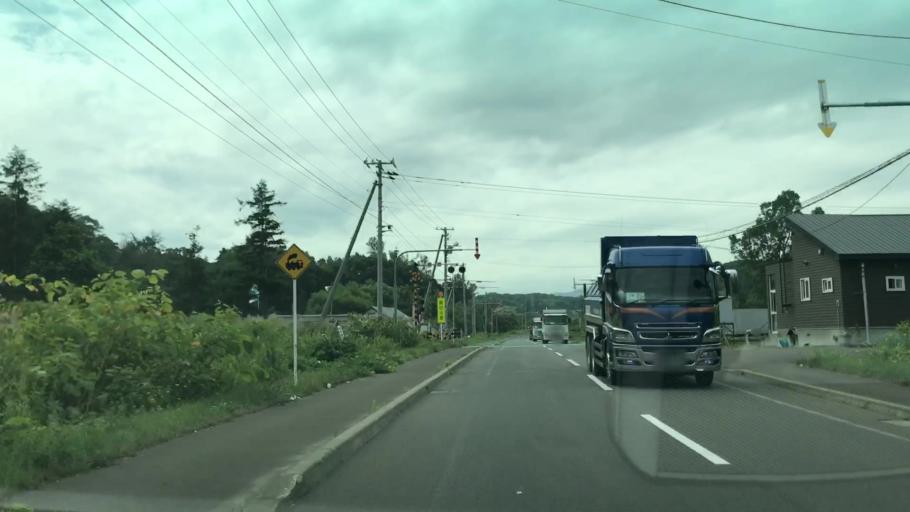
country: JP
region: Hokkaido
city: Yoichi
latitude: 43.1957
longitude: 140.8443
